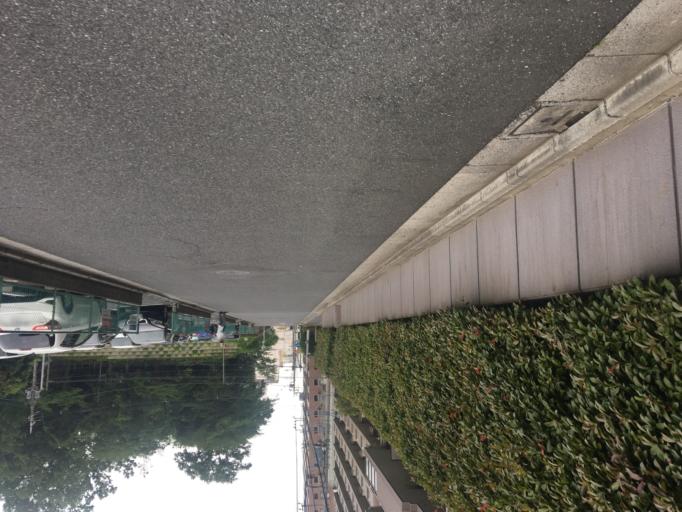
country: JP
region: Saitama
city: Shimotoda
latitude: 35.8451
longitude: 139.6669
